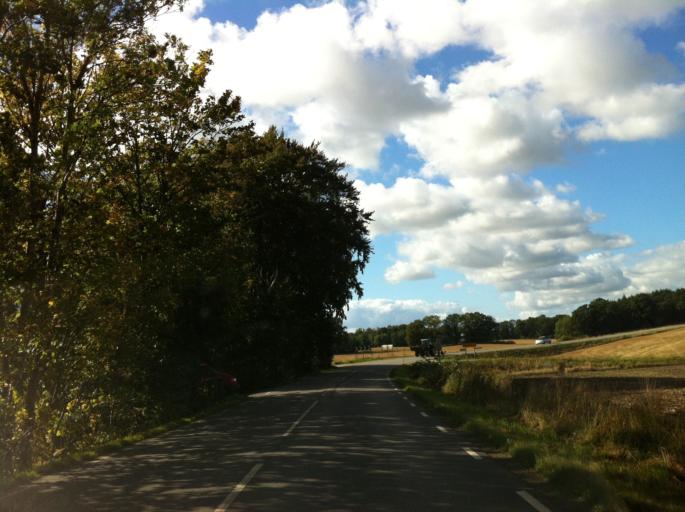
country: SE
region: Skane
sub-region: Tomelilla Kommun
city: Tomelilla
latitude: 55.6504
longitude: 13.9558
